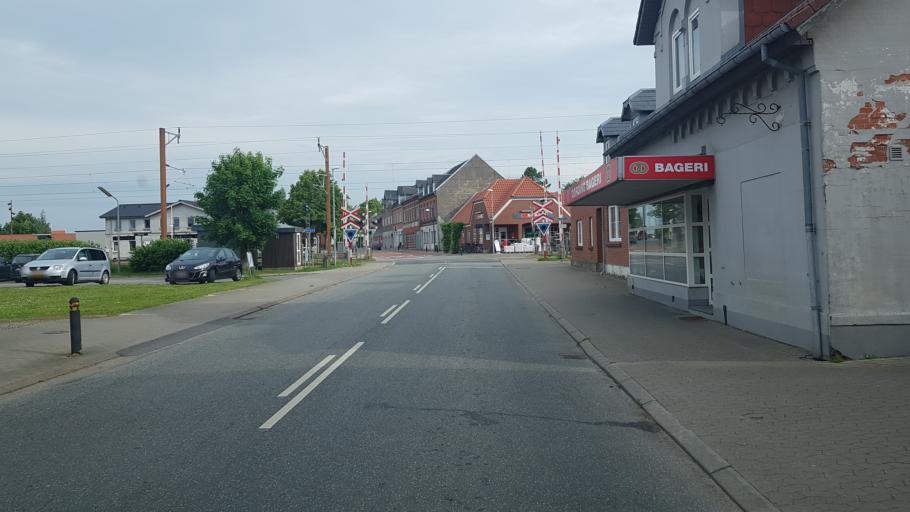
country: DK
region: South Denmark
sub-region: Esbjerg Kommune
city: Bramming
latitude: 55.4693
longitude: 8.8030
